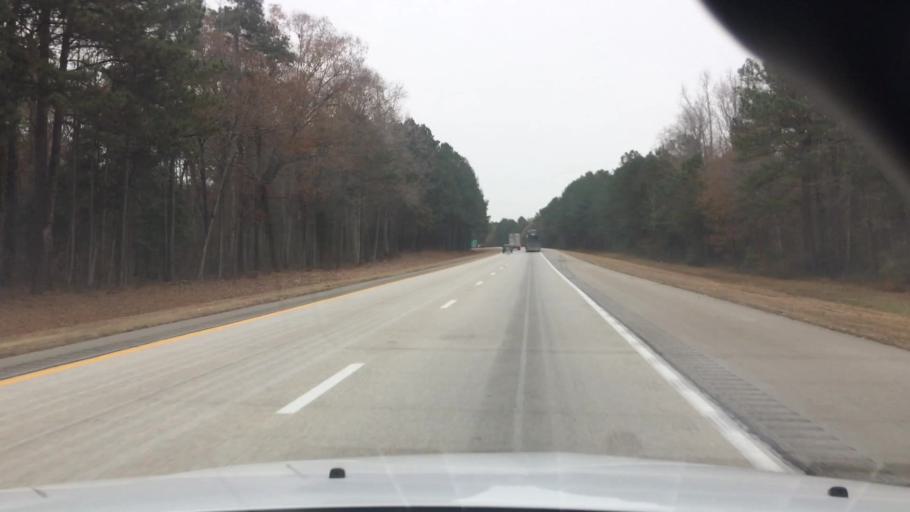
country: US
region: North Carolina
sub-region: Nash County
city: Nashville
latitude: 35.9392
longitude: -77.8962
